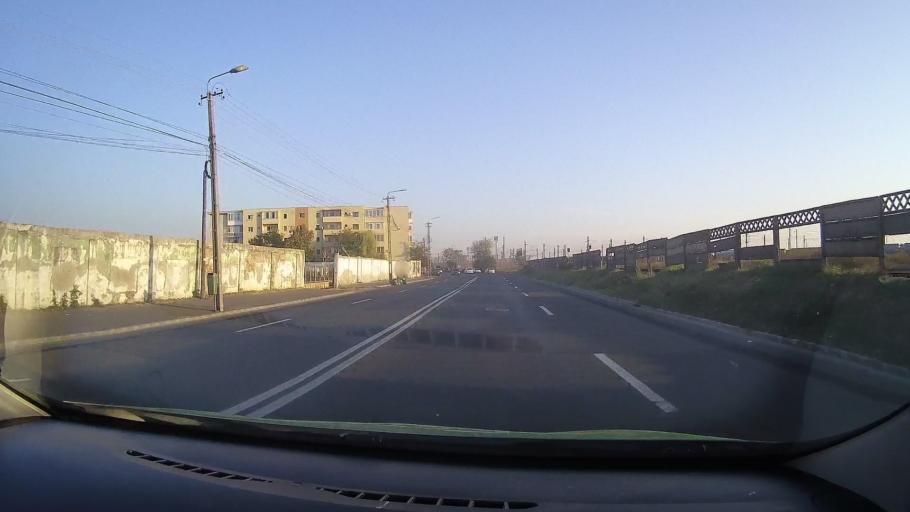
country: RO
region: Arad
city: Arad
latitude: 46.1948
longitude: 21.3205
